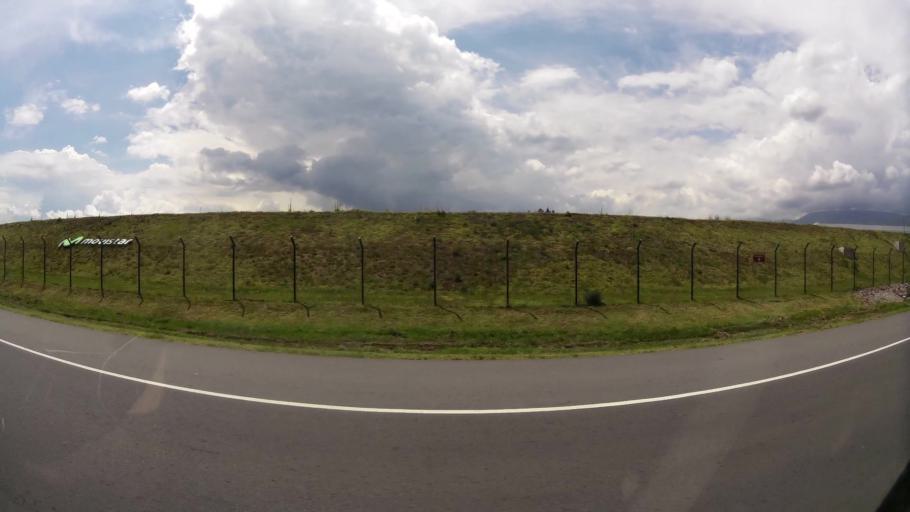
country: EC
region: Pichincha
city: Quito
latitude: -0.1511
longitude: -78.3515
